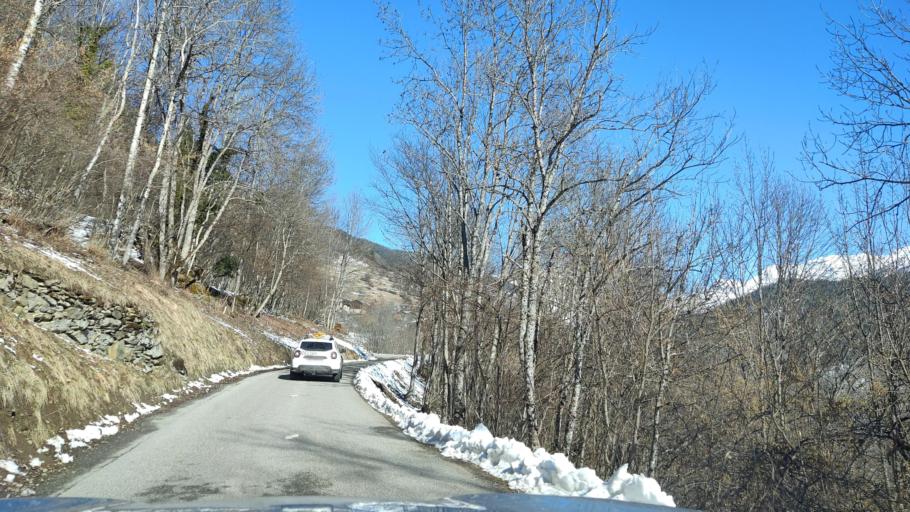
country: FR
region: Rhone-Alpes
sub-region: Departement de la Savoie
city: Aigueblanche
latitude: 45.5363
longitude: 6.4917
